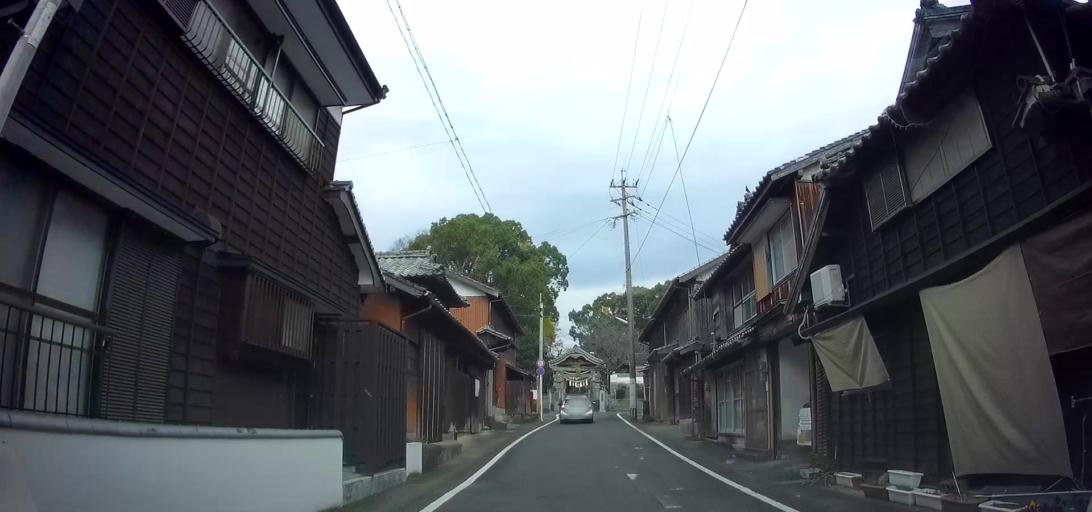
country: JP
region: Nagasaki
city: Shimabara
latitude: 32.6732
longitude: 130.3017
